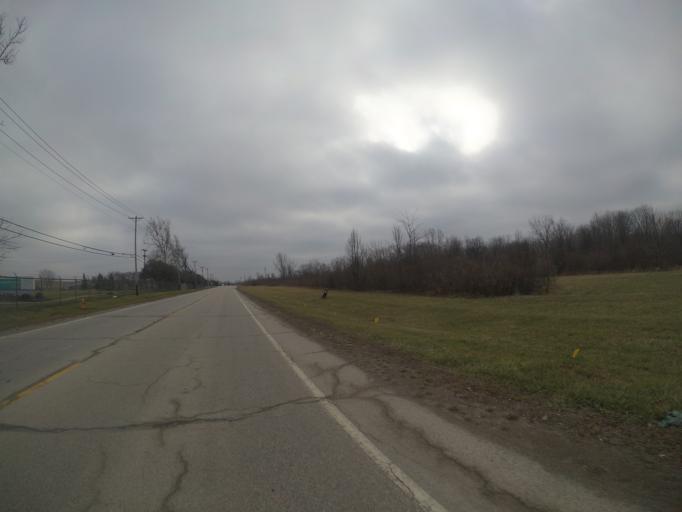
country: US
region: Ohio
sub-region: Wood County
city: Walbridge
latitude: 41.6108
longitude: -83.5124
